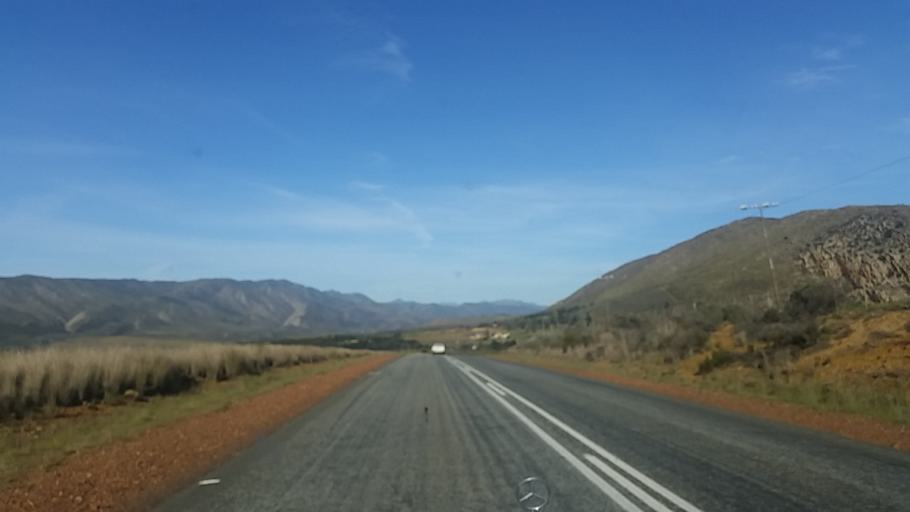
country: ZA
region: Western Cape
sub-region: Eden District Municipality
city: Knysna
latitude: -33.7723
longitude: 22.9468
